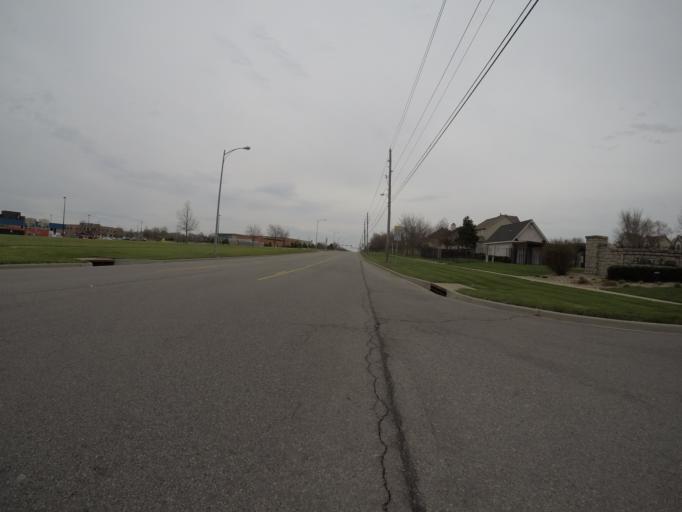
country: US
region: Kansas
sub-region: Johnson County
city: Olathe
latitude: 38.8691
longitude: -94.7642
